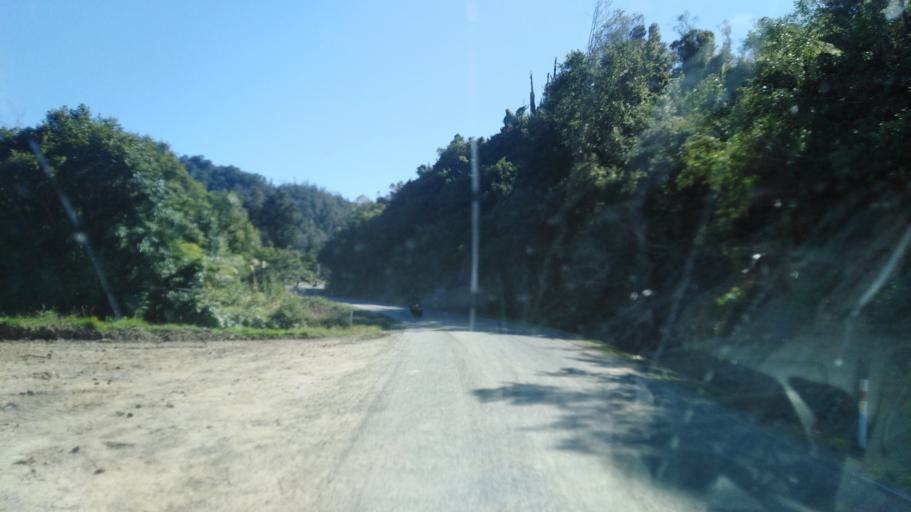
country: NZ
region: West Coast
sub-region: Buller District
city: Westport
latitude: -41.5310
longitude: 171.9935
